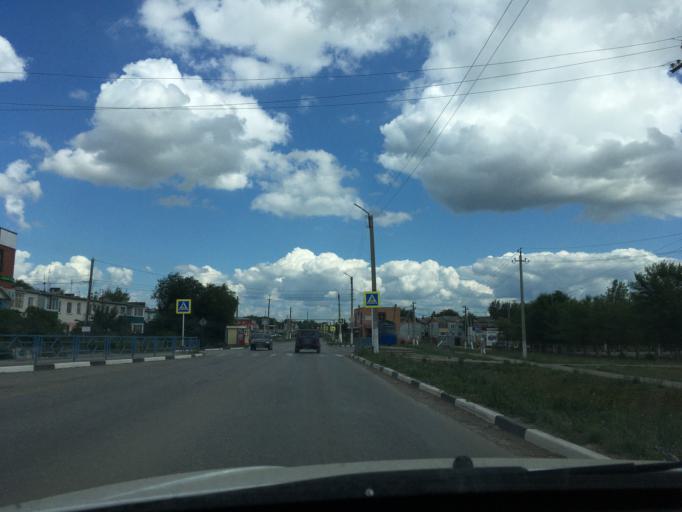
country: RU
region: Samara
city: Bezenchuk
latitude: 52.9913
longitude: 49.4365
